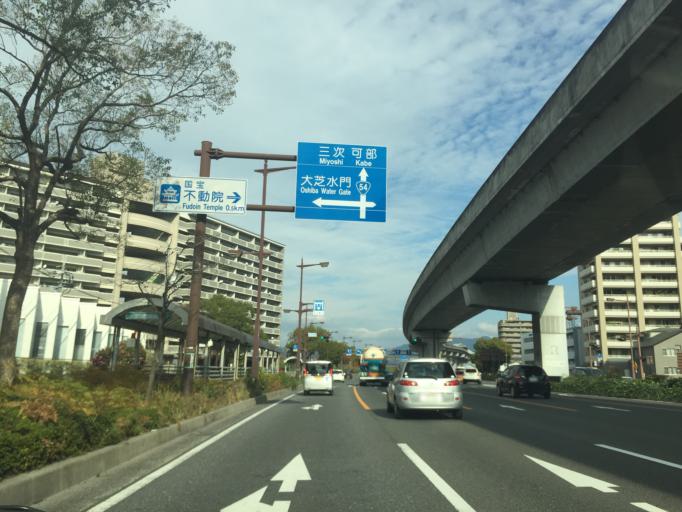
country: JP
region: Hiroshima
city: Hiroshima-shi
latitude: 34.4235
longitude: 132.4661
